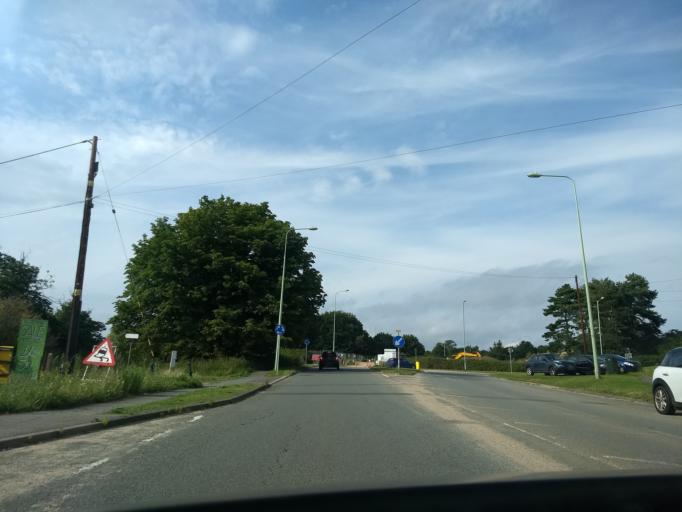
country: GB
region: England
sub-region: Suffolk
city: Woodbridge
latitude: 52.0820
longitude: 1.2873
